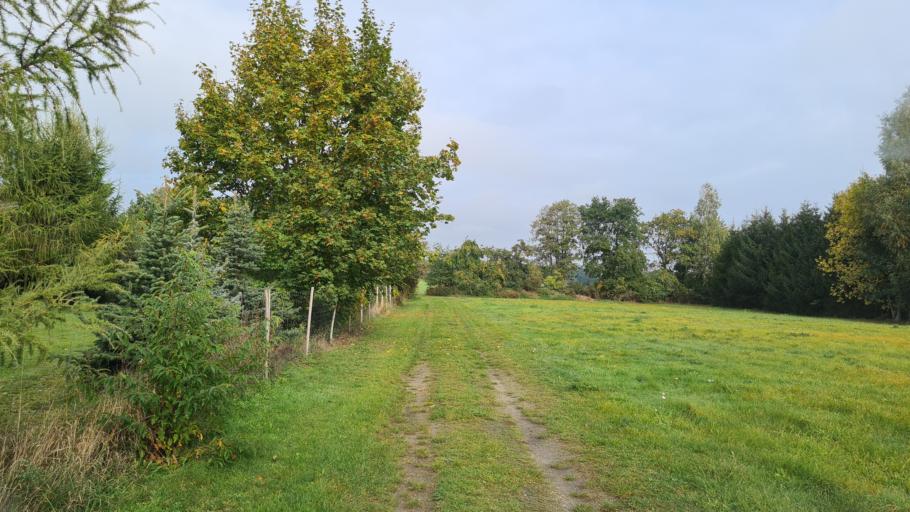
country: DE
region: Brandenburg
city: Schonewalde
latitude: 51.6923
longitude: 13.5362
